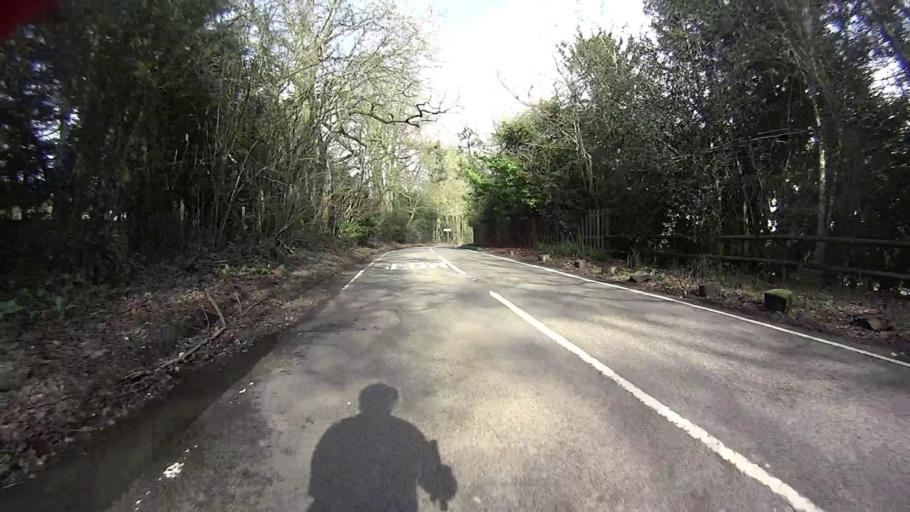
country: GB
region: England
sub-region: Surrey
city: Headley
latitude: 51.2621
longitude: -0.2674
